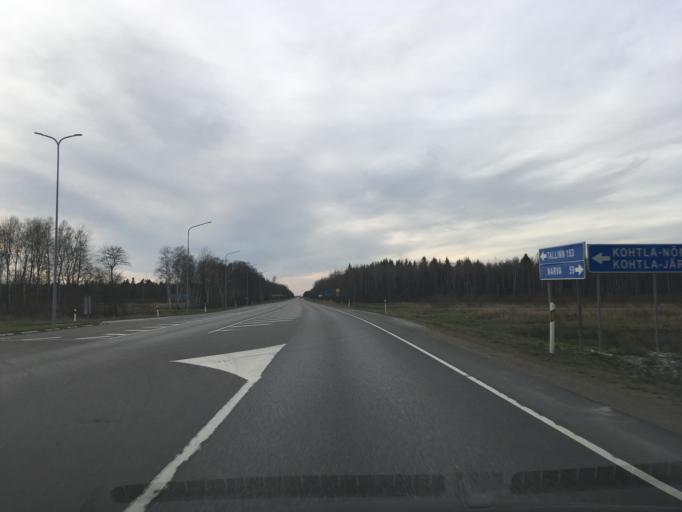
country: EE
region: Ida-Virumaa
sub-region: Kohtla-Jaerve linn
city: Kohtla-Jarve
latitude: 59.4209
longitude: 27.2750
